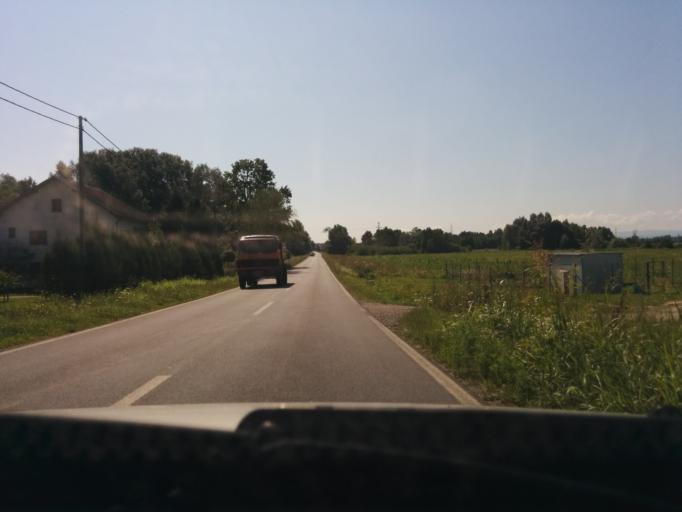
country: HR
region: Sisacko-Moslavacka
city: Lipovljani
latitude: 45.3864
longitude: 16.9031
